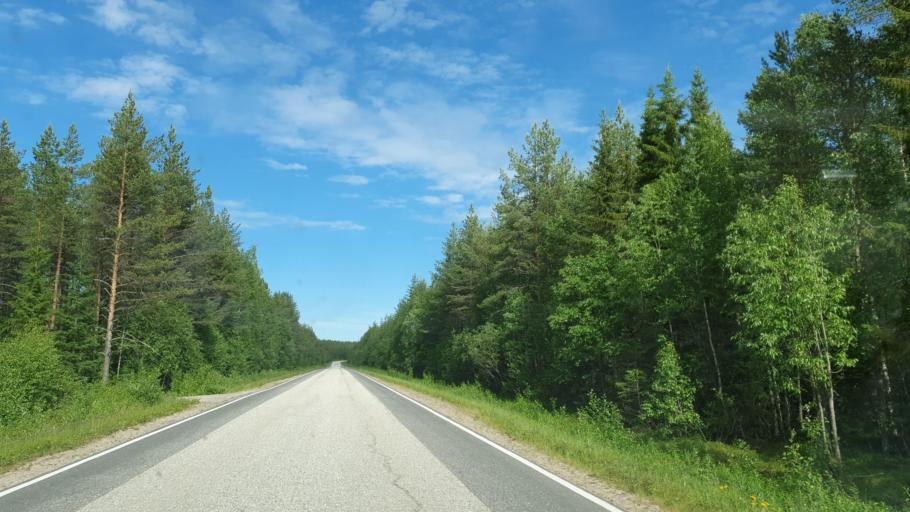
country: FI
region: Kainuu
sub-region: Kehys-Kainuu
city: Suomussalmi
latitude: 64.5904
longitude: 29.0774
